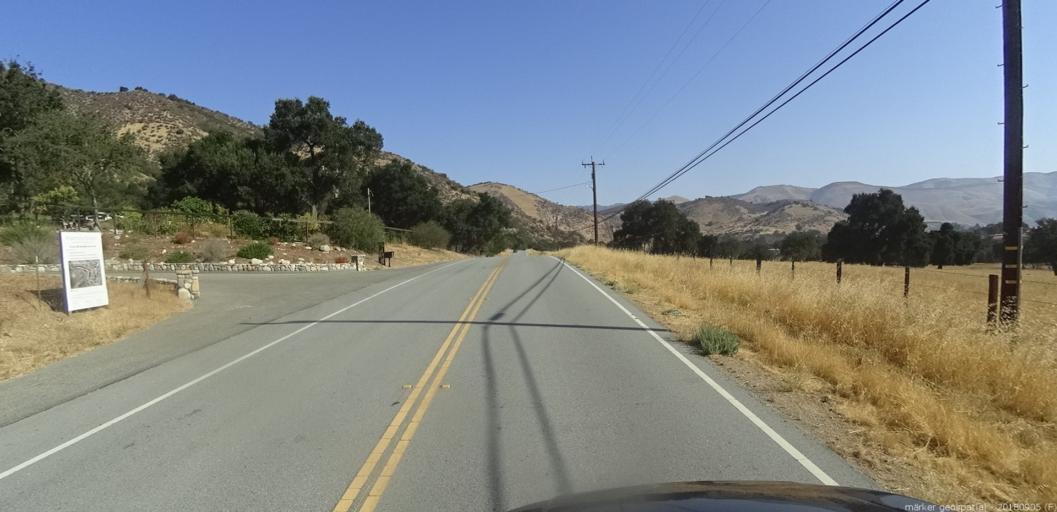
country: US
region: California
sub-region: Monterey County
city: Greenfield
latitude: 36.2455
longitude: -121.4323
